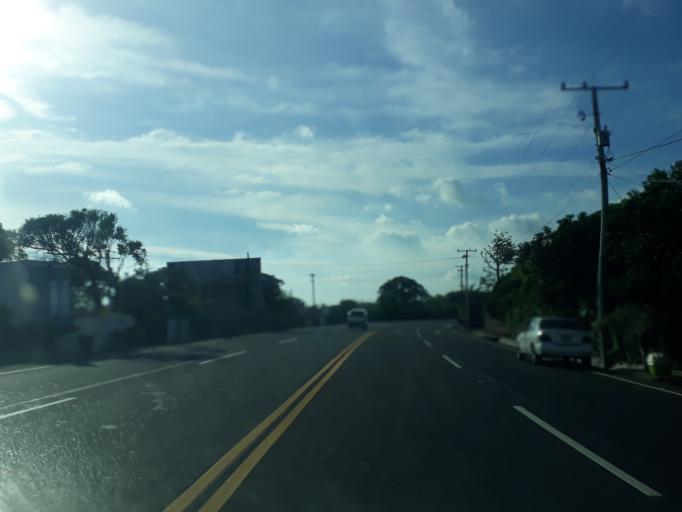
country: NI
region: Carazo
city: Diriamba
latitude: 11.9068
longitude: -86.2620
